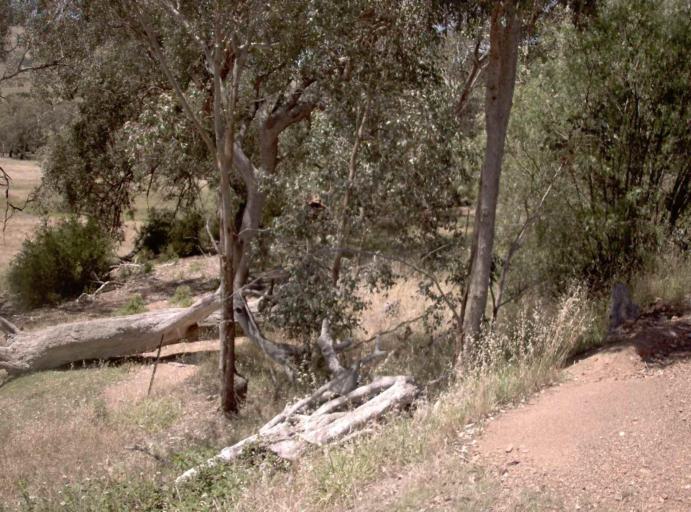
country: AU
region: Victoria
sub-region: East Gippsland
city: Bairnsdale
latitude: -37.2078
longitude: 147.7181
